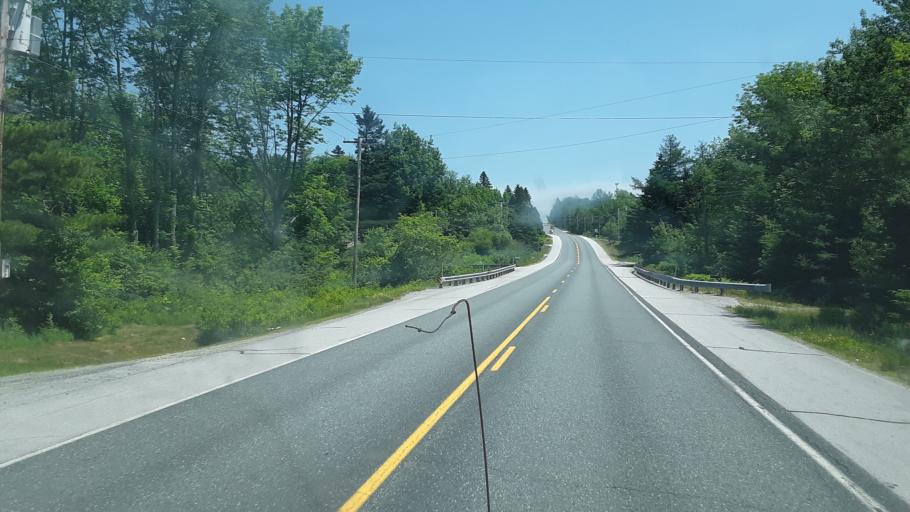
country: US
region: Maine
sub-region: Hancock County
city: Hancock
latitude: 44.5384
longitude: -68.3074
